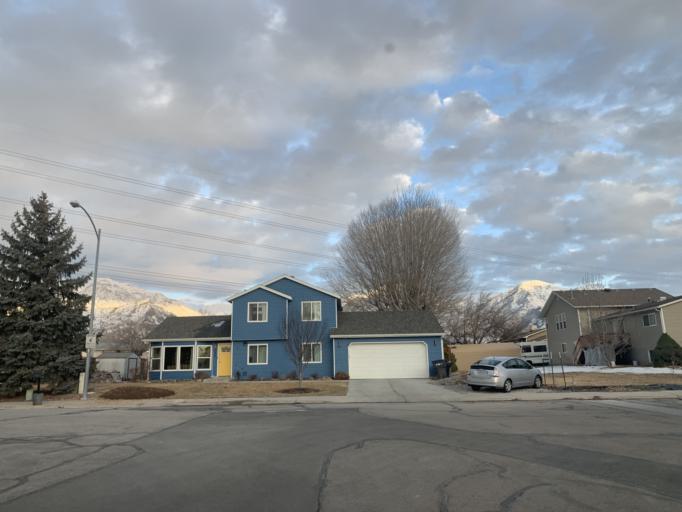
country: US
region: Utah
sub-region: Utah County
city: Provo
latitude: 40.2446
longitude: -111.7038
